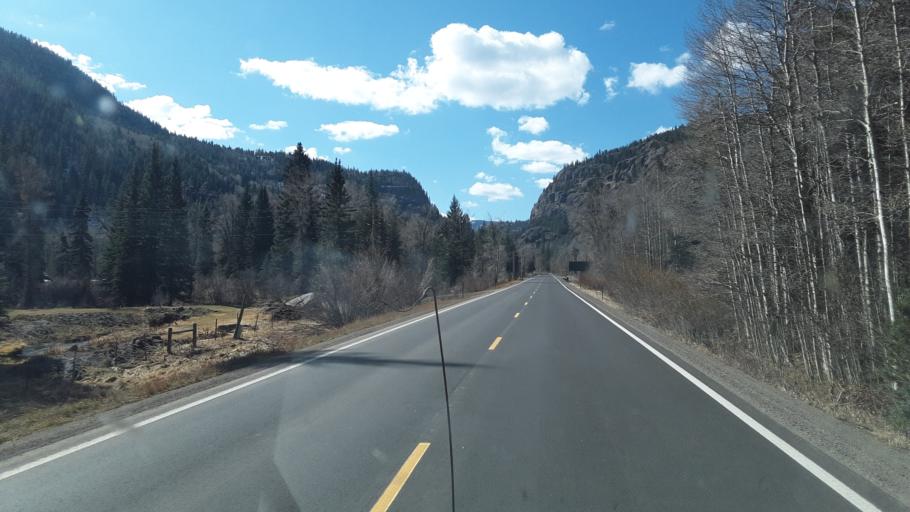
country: US
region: Colorado
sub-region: Mineral County
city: Creede
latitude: 37.5766
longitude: -106.7509
